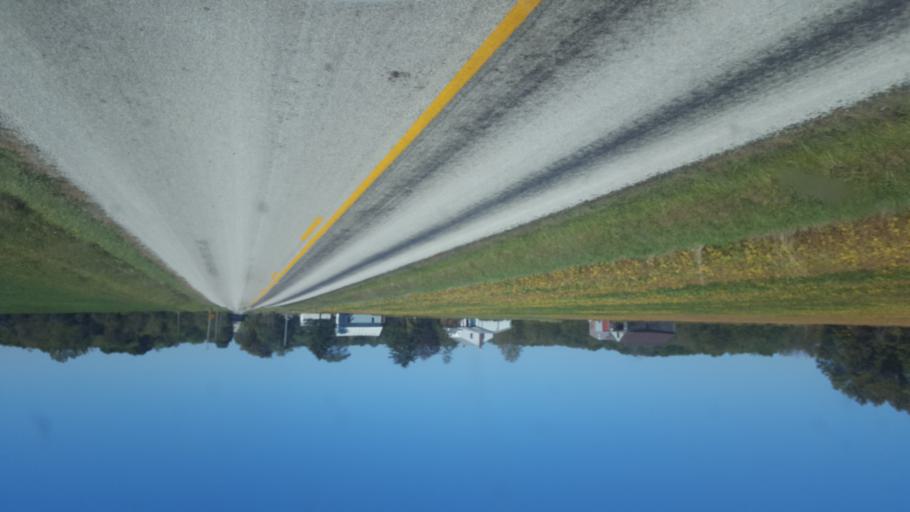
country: US
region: Ohio
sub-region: Ashland County
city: Ashland
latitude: 40.9927
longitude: -82.2577
